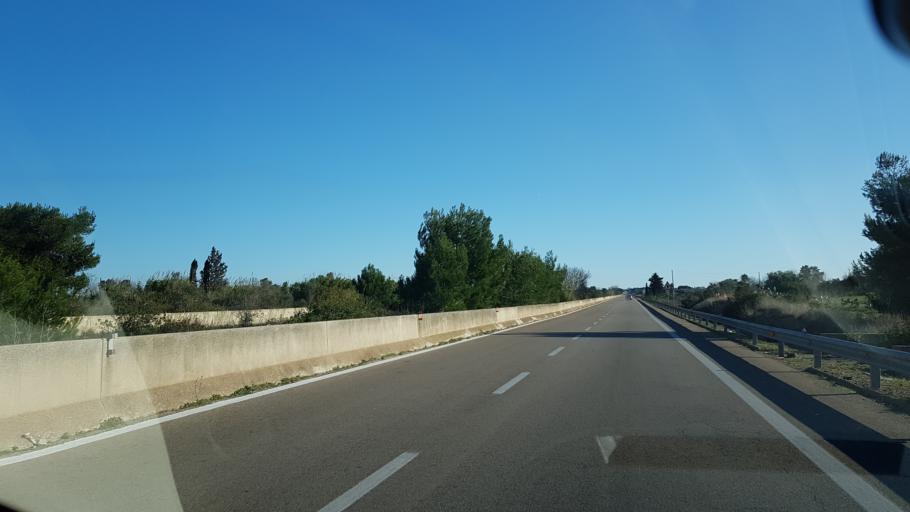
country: IT
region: Apulia
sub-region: Provincia di Lecce
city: Alezio
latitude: 40.0249
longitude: 18.0371
